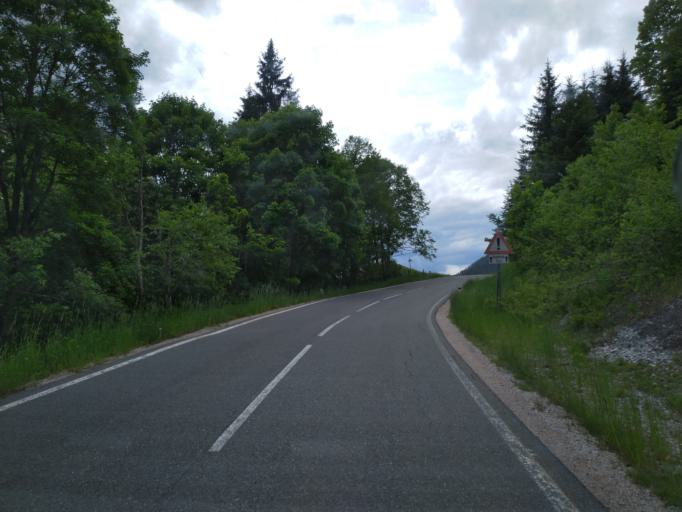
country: AT
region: Salzburg
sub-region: Politischer Bezirk Sankt Johann im Pongau
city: Filzmoos
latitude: 47.4365
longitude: 13.5739
